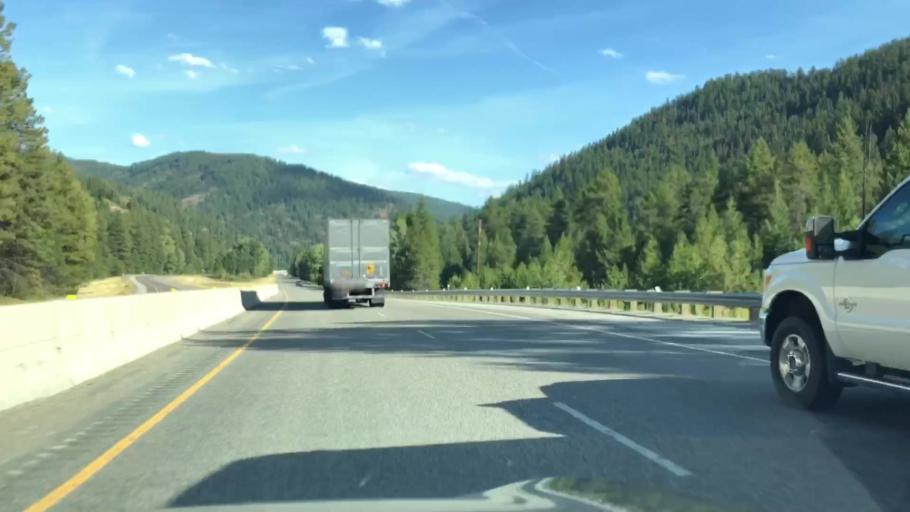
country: US
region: Montana
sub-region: Sanders County
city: Thompson Falls
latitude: 47.3599
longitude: -115.3170
